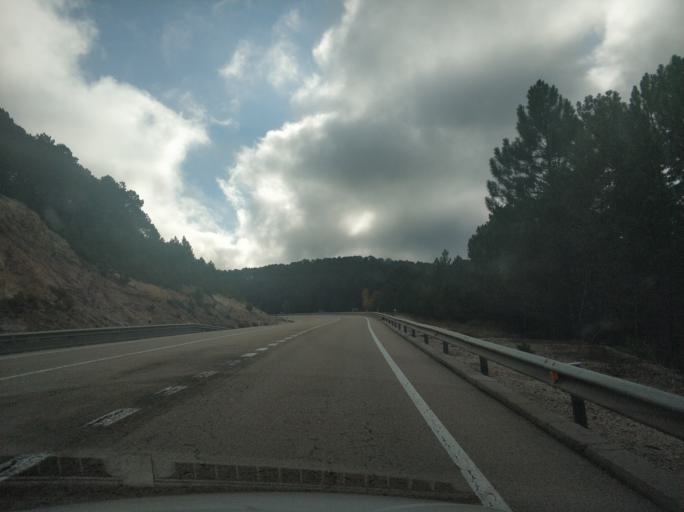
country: ES
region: Castille and Leon
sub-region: Provincia de Soria
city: Navaleno
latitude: 41.8292
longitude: -2.9680
